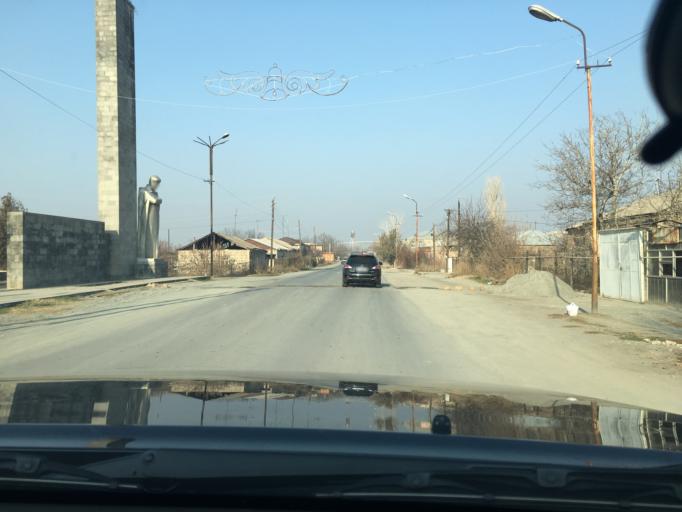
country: AM
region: Armavir
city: Aygeshat
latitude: 40.0852
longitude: 44.0503
